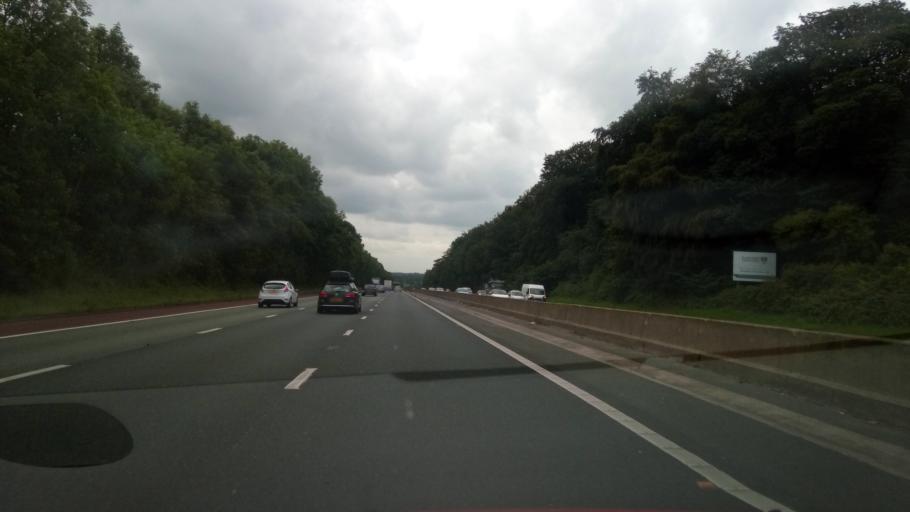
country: GB
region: England
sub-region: Lancashire
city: Galgate
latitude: 54.0149
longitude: -2.7819
